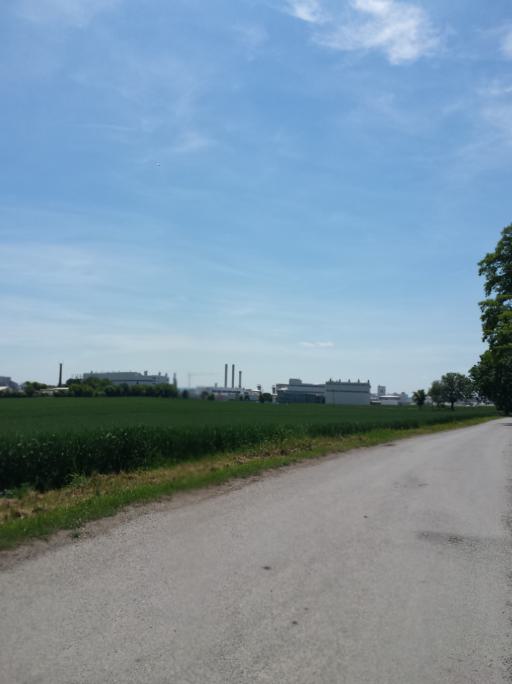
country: CZ
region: South Moravian
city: Jaroslavice
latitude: 48.7281
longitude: 16.2743
